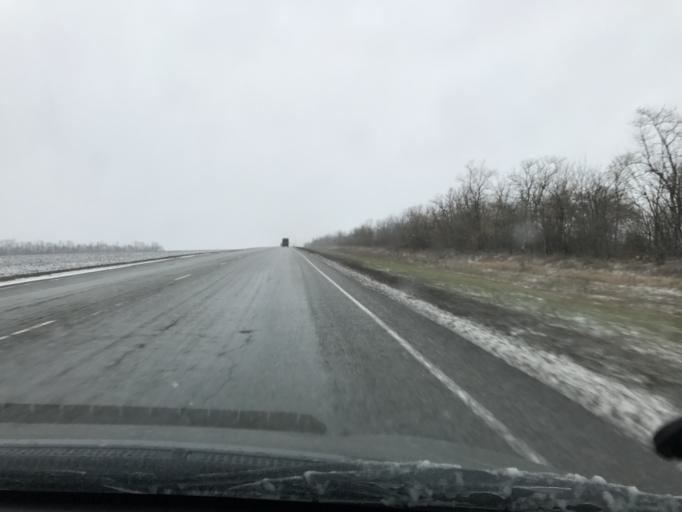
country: RU
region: Rostov
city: Mechetinskaya
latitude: 46.7024
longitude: 40.5034
